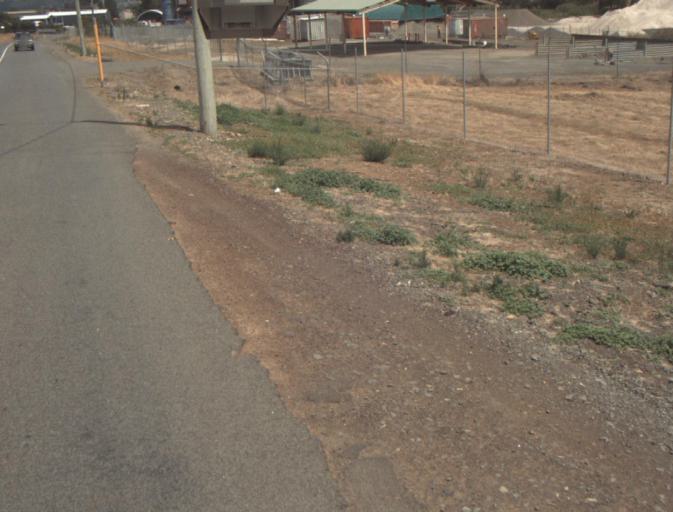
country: AU
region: Tasmania
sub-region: Launceston
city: Newnham
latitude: -41.3997
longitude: 147.1487
